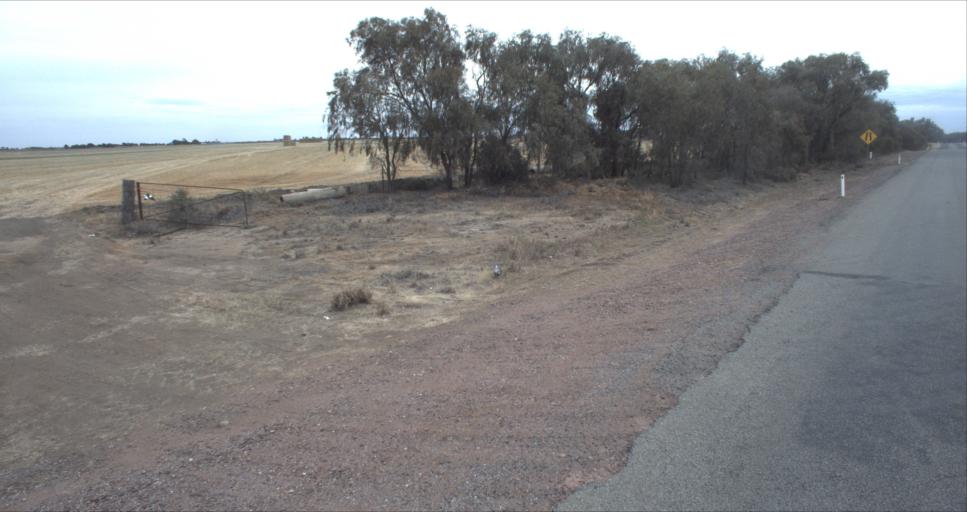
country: AU
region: New South Wales
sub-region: Leeton
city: Leeton
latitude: -34.4797
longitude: 146.3991
